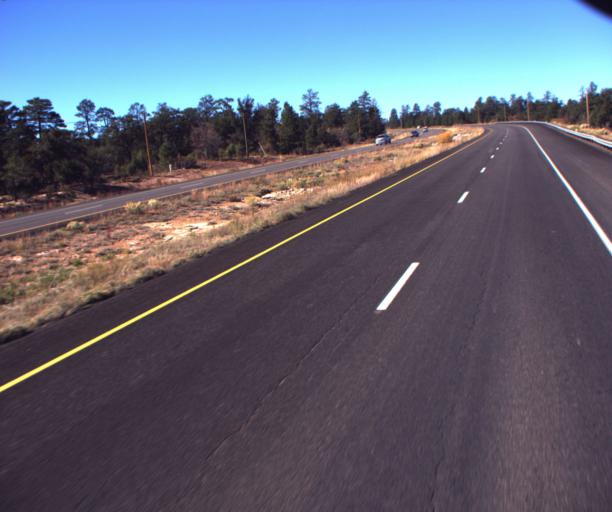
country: US
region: Arizona
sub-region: Apache County
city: Saint Michaels
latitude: 35.6678
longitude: -109.1639
